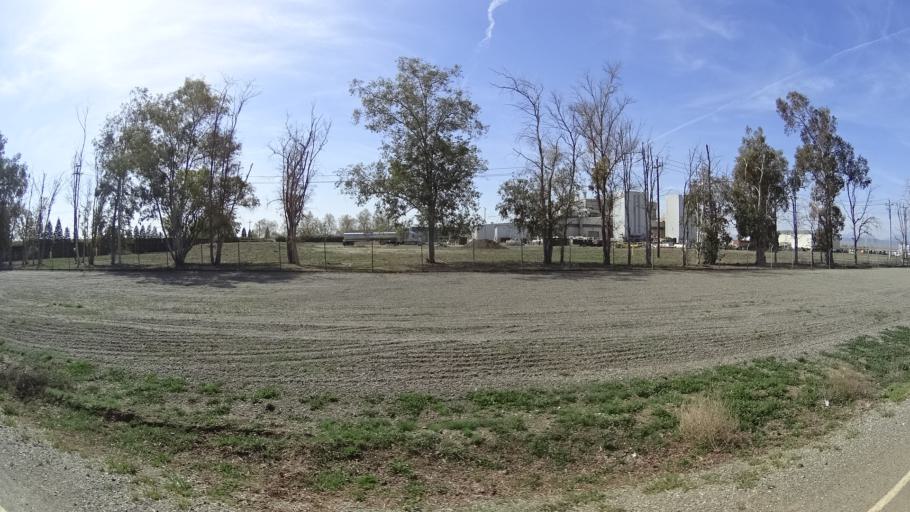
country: US
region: California
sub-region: Glenn County
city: Willows
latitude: 39.5388
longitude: -122.2613
